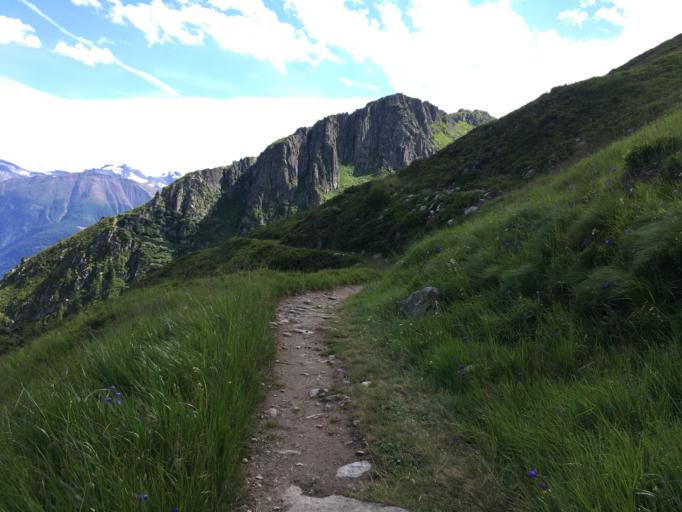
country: CH
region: Valais
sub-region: Goms District
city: Fiesch
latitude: 46.4406
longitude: 8.1202
